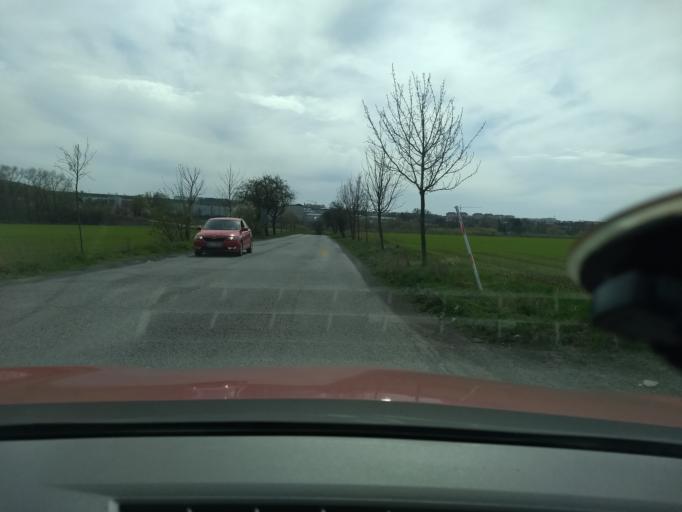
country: CZ
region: Central Bohemia
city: Hostivice
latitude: 50.0692
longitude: 14.2353
